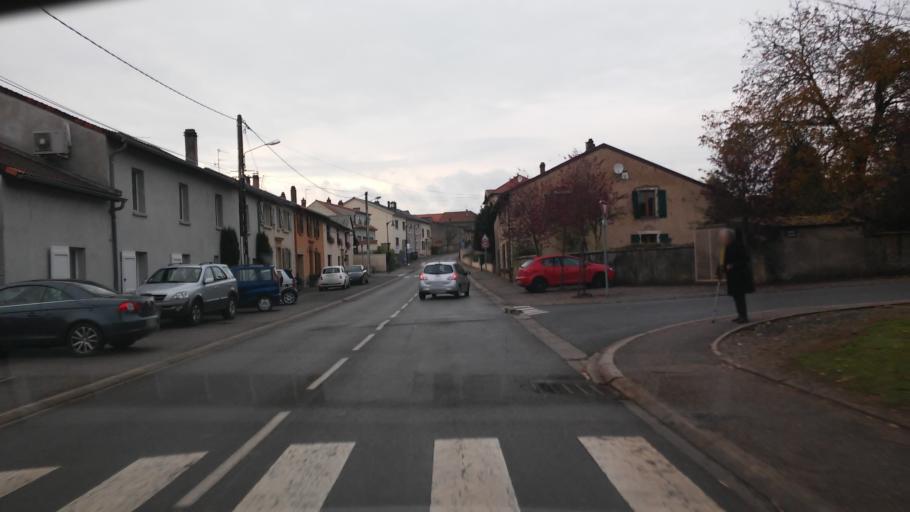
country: FR
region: Lorraine
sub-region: Departement de la Moselle
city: Ennery
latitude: 49.2055
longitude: 6.2361
